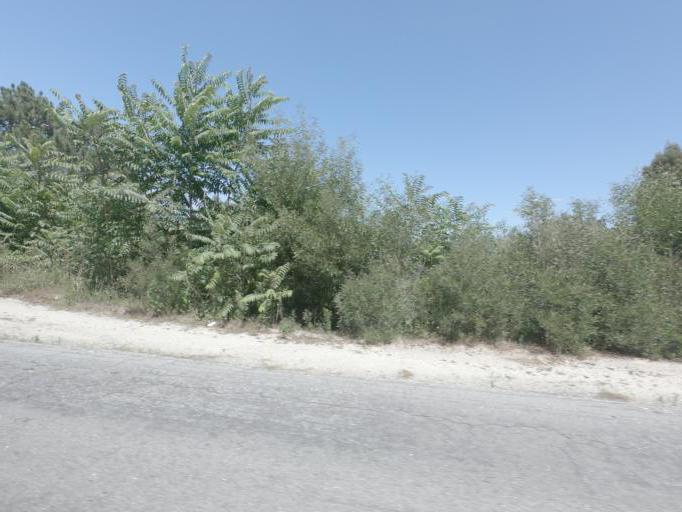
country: PT
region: Porto
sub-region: Amarante
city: Amarante
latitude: 41.2705
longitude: -8.1015
